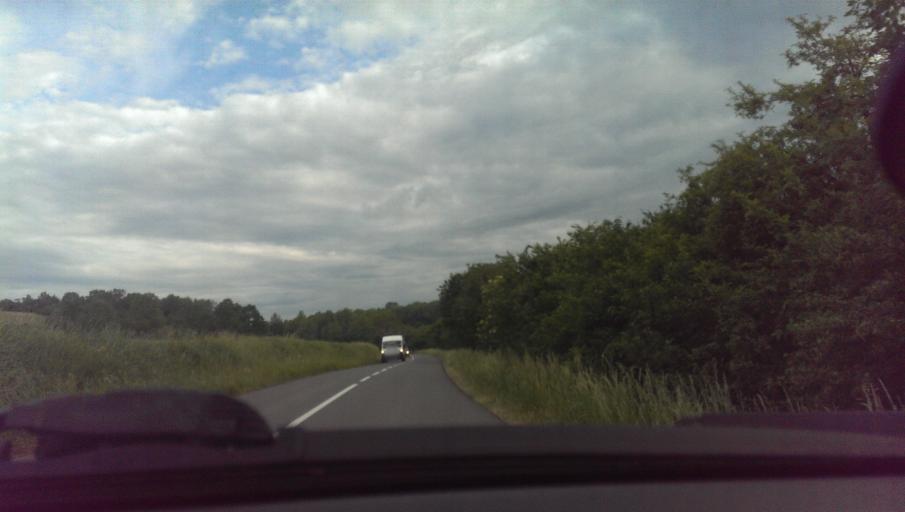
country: CZ
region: Zlin
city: Kvasice
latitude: 49.2284
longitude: 17.4890
